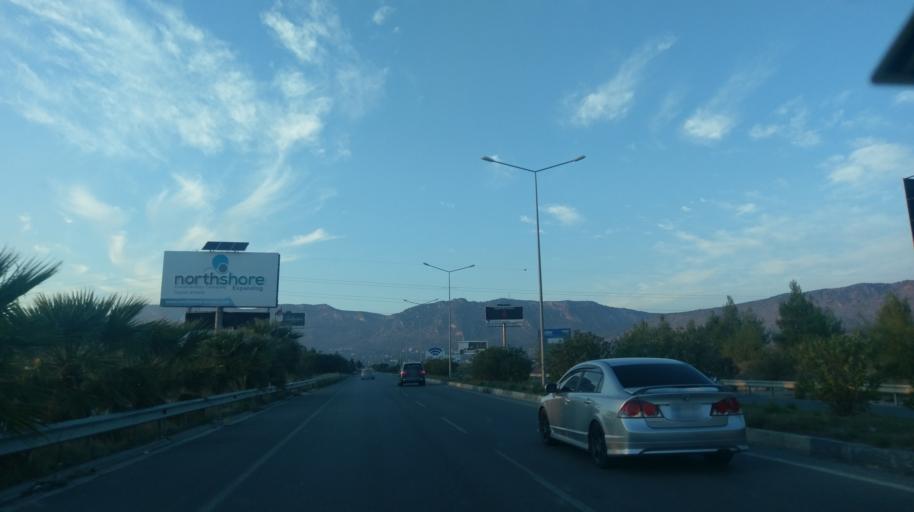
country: CY
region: Keryneia
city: Kyrenia
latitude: 35.2603
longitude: 33.2969
